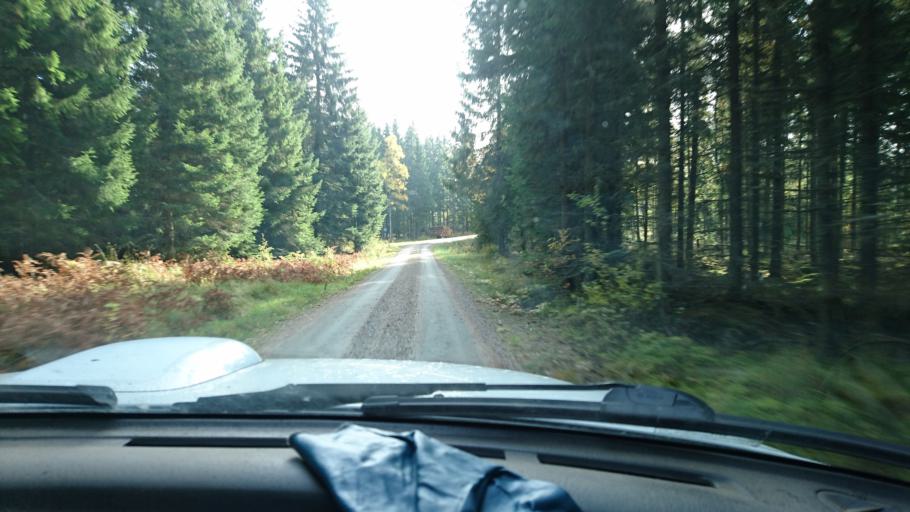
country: SE
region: Vaestra Goetaland
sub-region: Ulricehamns Kommun
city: Ulricehamn
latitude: 57.9463
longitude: 13.5391
